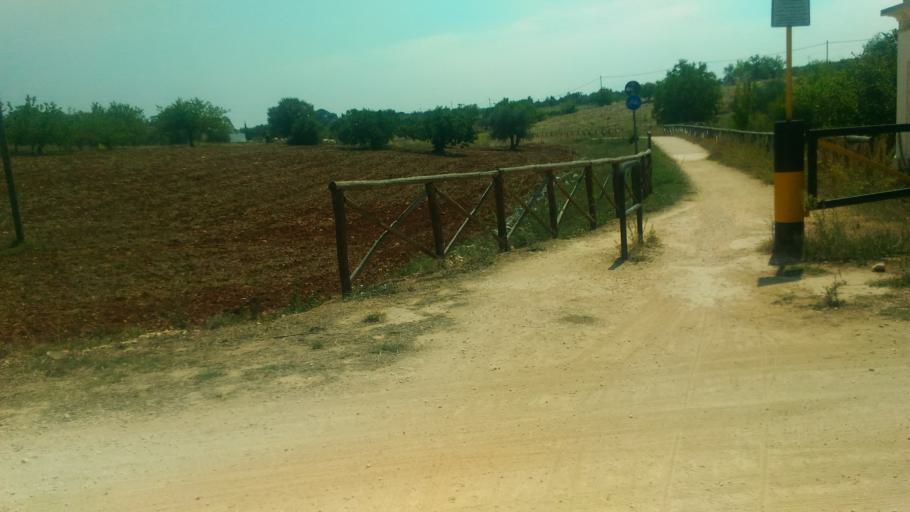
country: IT
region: Apulia
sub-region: Provincia di Brindisi
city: Cisternino
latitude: 40.7240
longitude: 17.3962
